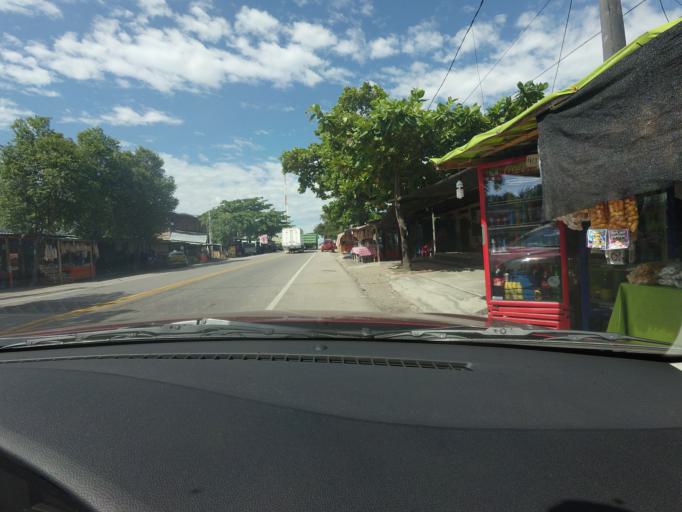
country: CO
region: Tolima
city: Saldana
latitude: 3.8192
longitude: -75.0632
